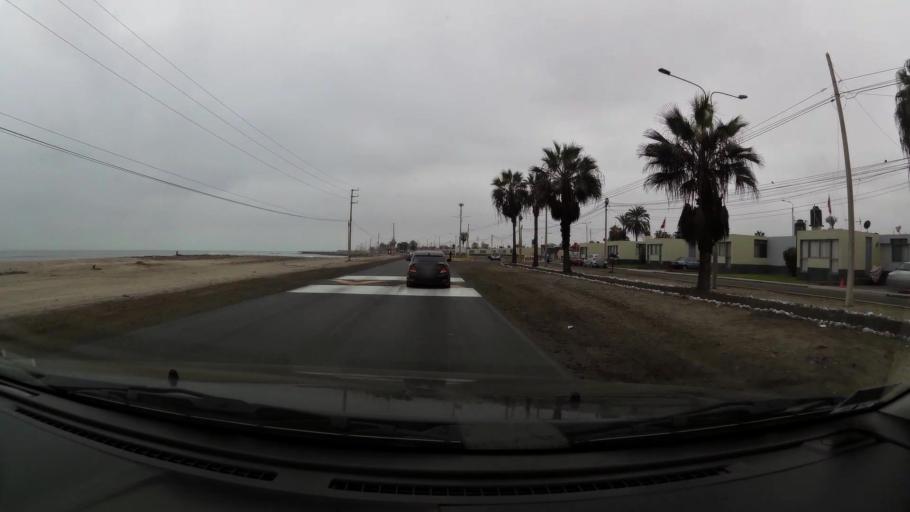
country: PE
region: Ica
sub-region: Provincia de Pisco
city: Pisco
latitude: -13.7427
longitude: -76.2269
